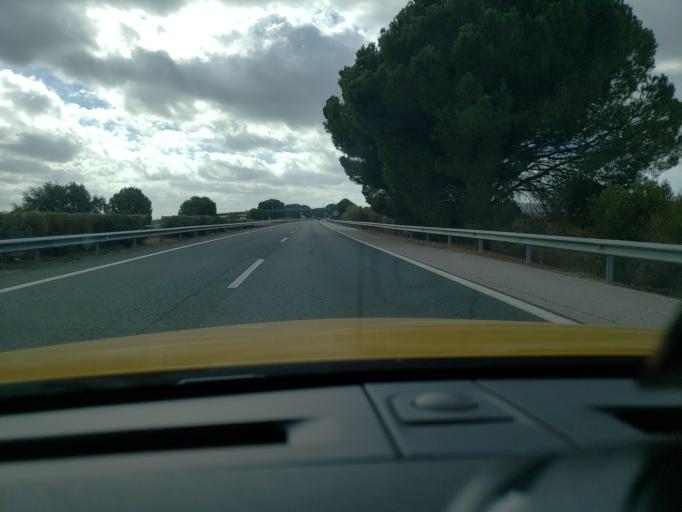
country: ES
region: Andalusia
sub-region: Provincia de Sevilla
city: Las Cabezas de San Juan
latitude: 37.0241
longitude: -5.9286
